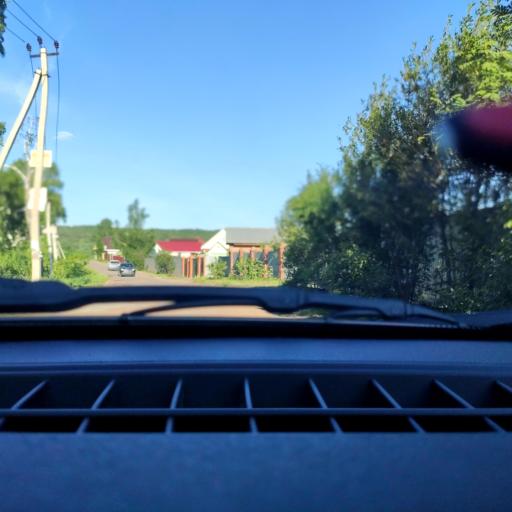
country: RU
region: Bashkortostan
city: Avdon
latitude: 54.4618
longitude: 55.8433
